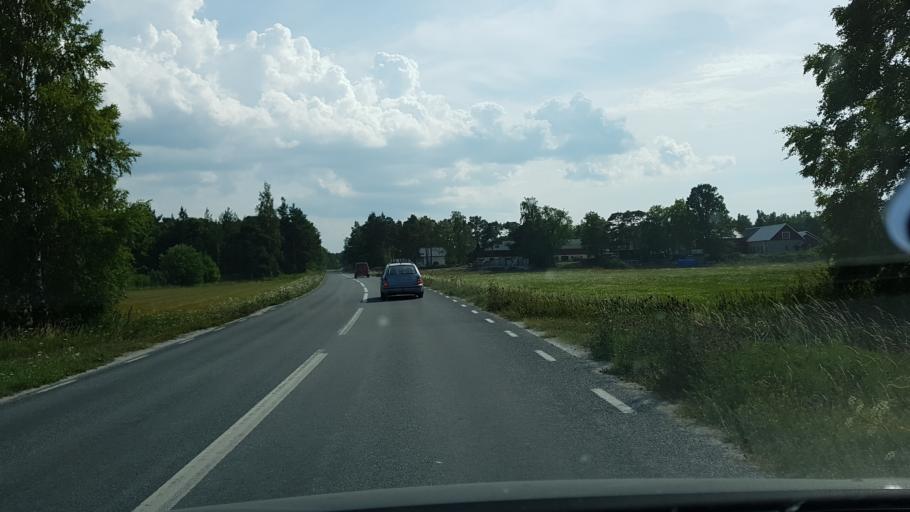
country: SE
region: Gotland
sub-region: Gotland
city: Visby
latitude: 57.7864
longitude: 18.4564
